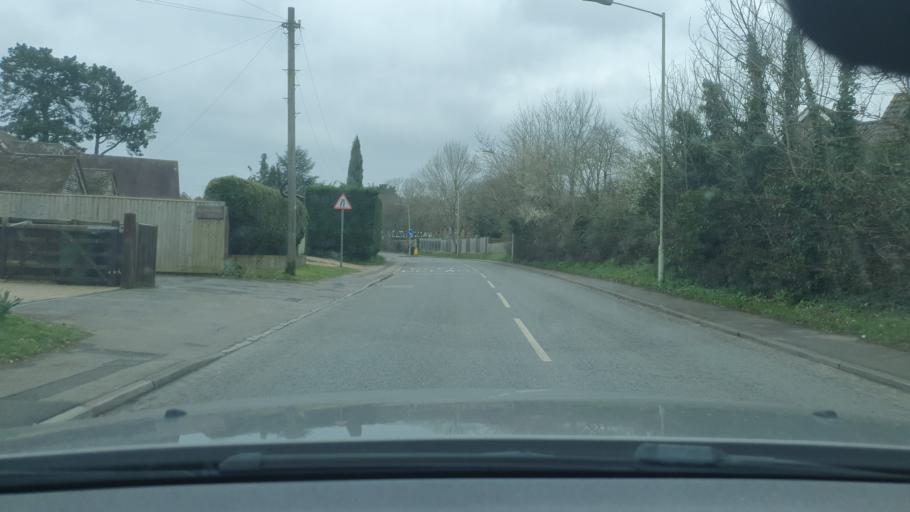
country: GB
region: England
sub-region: West Berkshire
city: Tilehurst
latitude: 51.4793
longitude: -1.0510
